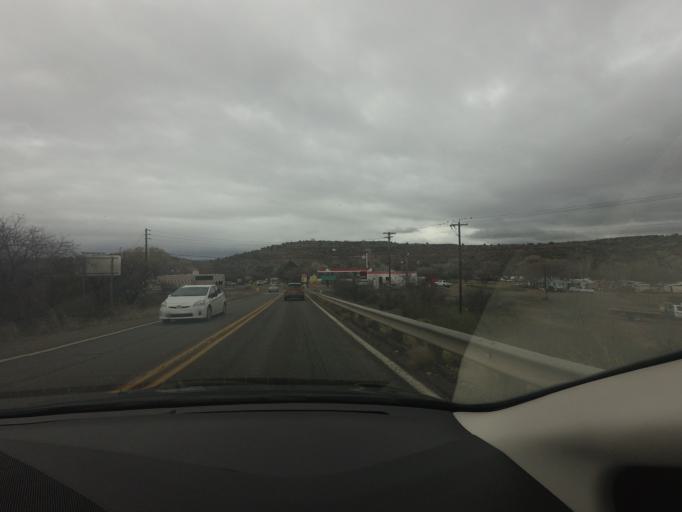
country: US
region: Arizona
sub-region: Yavapai County
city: Lake Montezuma
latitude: 34.6379
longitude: -111.8158
